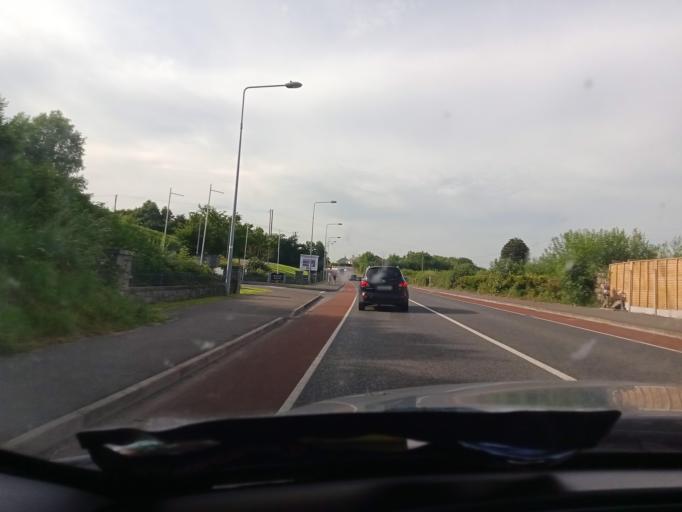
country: IE
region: Ulster
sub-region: An Cabhan
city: Cavan
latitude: 53.9775
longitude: -7.3545
